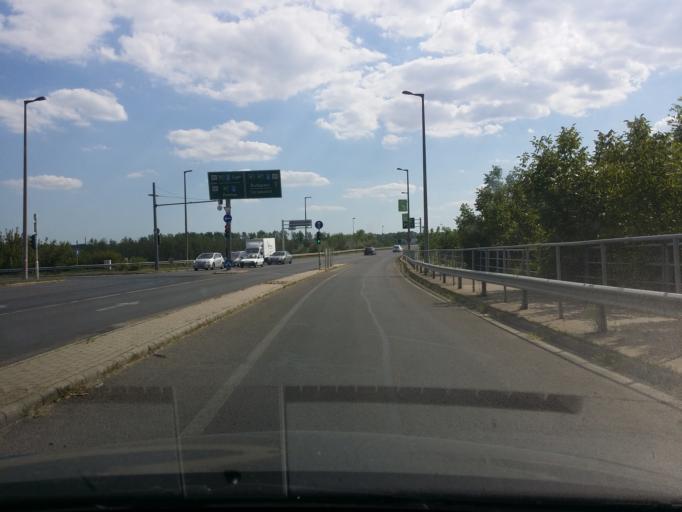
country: HU
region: Pest
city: Budaors
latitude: 47.4542
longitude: 18.9488
